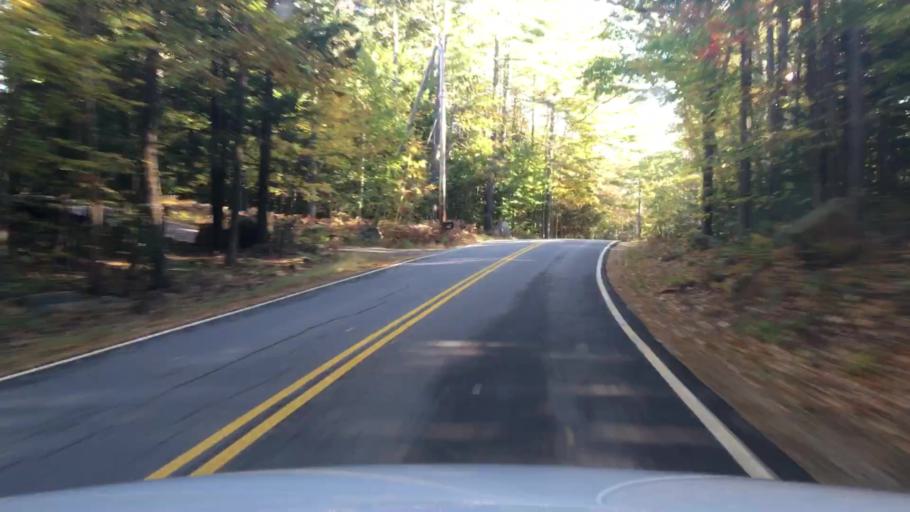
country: US
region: New Hampshire
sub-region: Strafford County
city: Barrington
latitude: 43.1765
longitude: -71.0440
